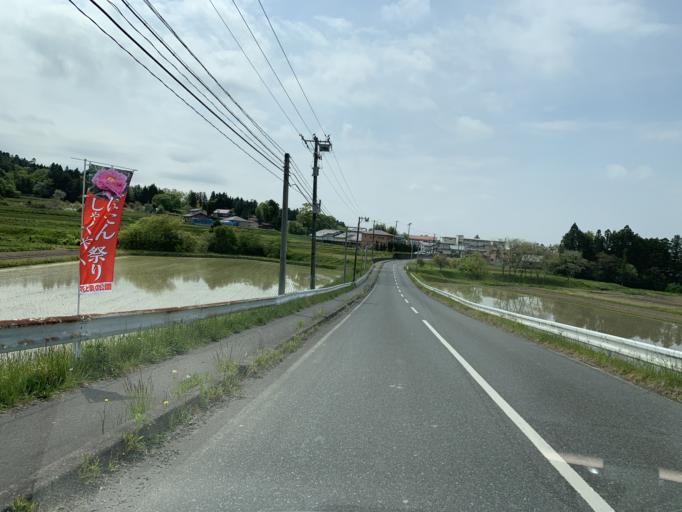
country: JP
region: Iwate
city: Ichinoseki
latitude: 38.8305
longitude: 141.2014
